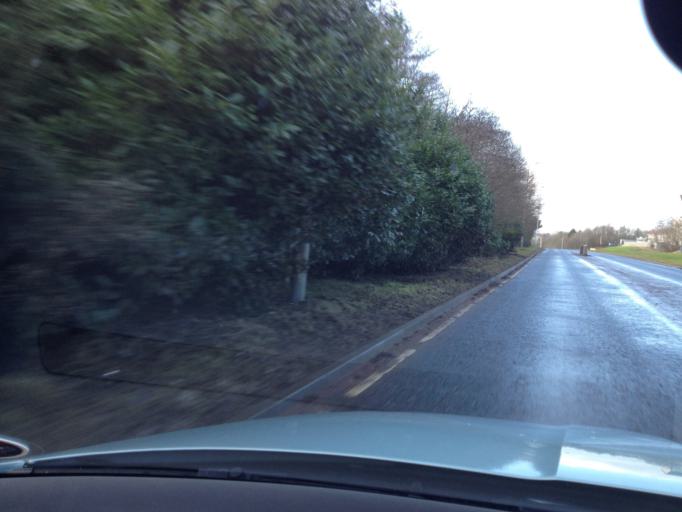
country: GB
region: Scotland
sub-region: West Lothian
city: Livingston
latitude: 55.8950
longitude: -3.5206
